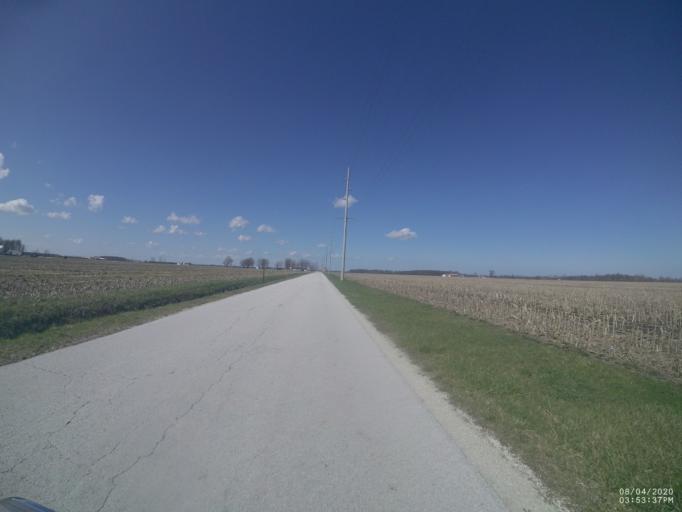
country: US
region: Ohio
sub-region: Sandusky County
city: Ballville
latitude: 41.2764
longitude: -83.1884
